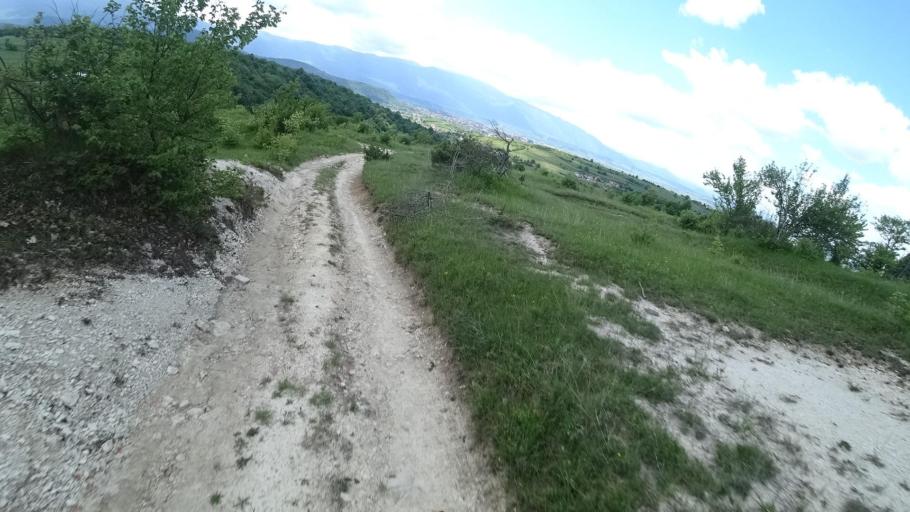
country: BA
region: Federation of Bosnia and Herzegovina
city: Bihac
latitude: 44.8154
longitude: 15.9208
